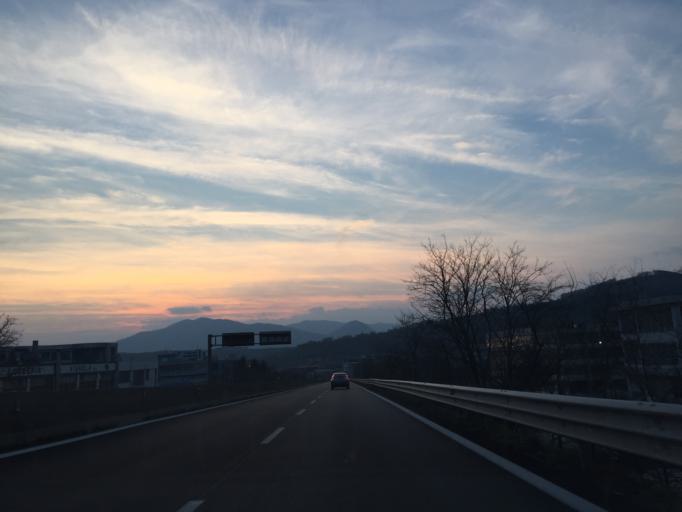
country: IT
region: Campania
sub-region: Provincia di Avellino
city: Solofra
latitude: 40.8337
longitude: 14.8328
